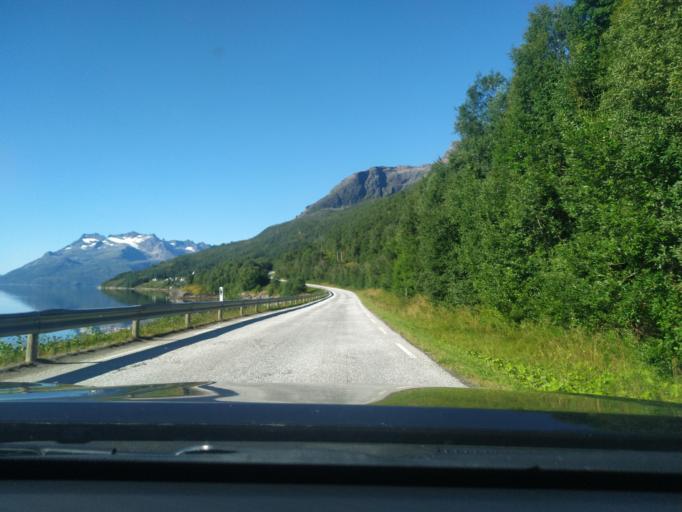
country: NO
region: Troms
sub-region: Dyroy
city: Brostadbotn
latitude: 68.9315
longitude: 17.6733
